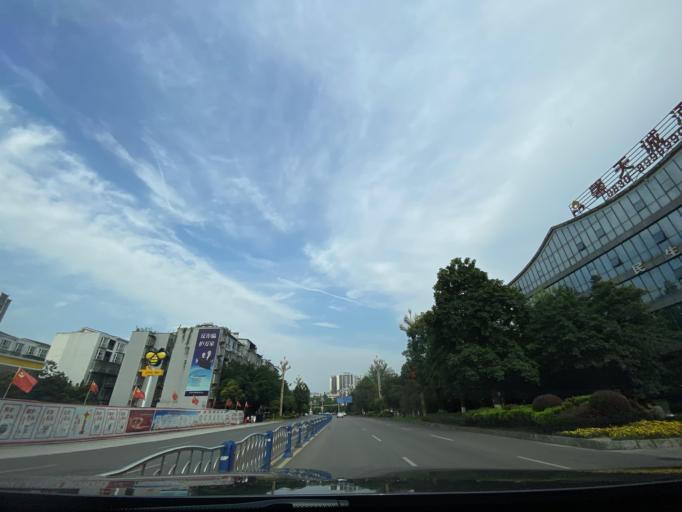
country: CN
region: Sichuan
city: Fuji
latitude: 29.1523
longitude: 105.3484
